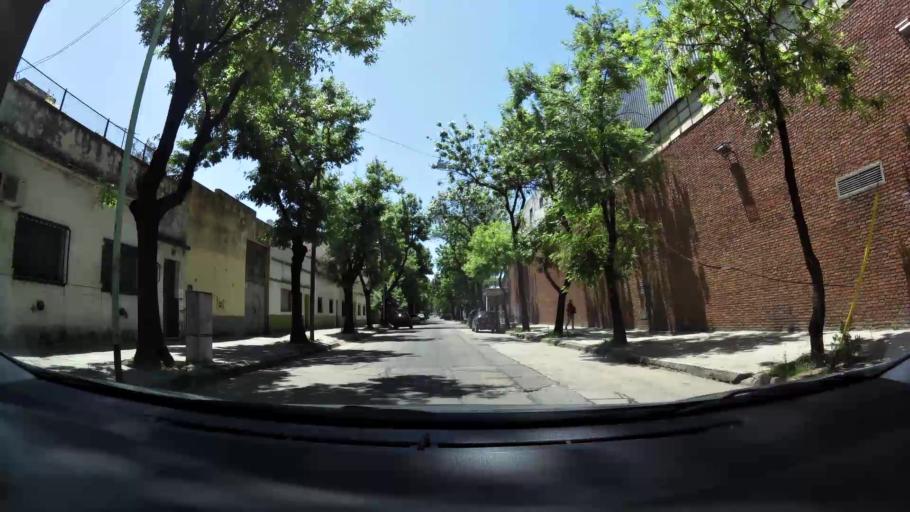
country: AR
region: Buenos Aires
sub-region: Partido de Avellaneda
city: Avellaneda
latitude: -34.6538
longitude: -58.3921
